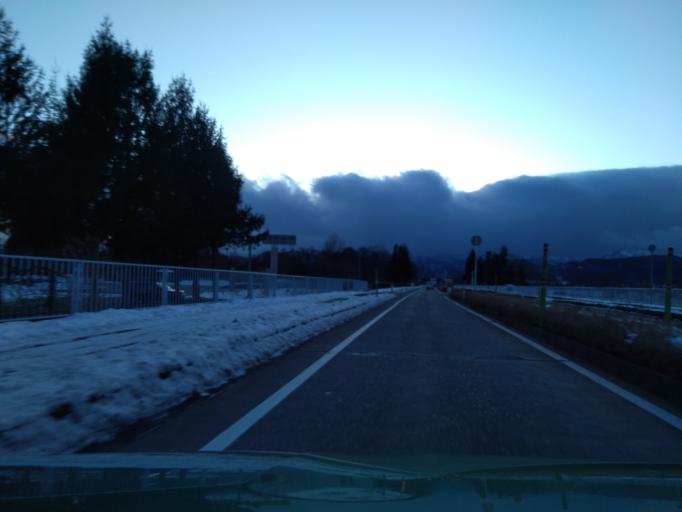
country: JP
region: Iwate
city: Shizukuishi
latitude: 39.7017
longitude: 140.9624
